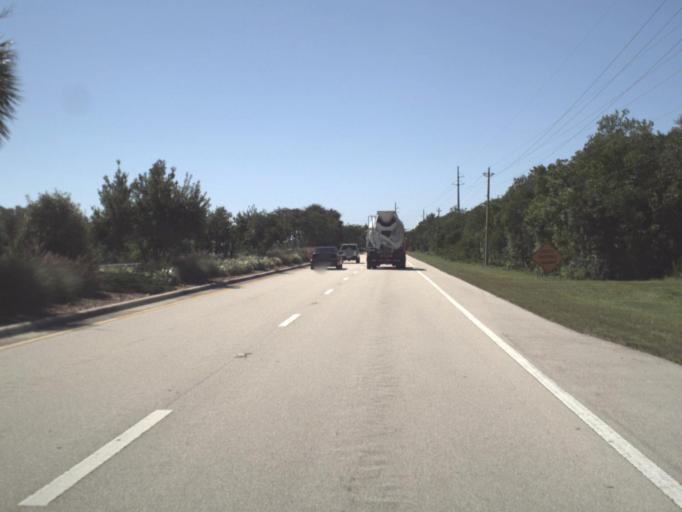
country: US
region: Florida
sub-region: Collier County
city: Marco
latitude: 25.9742
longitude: -81.7062
